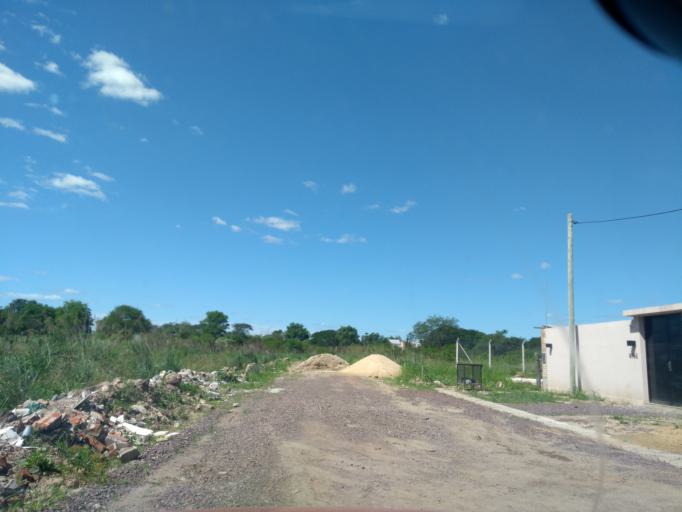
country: AR
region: Chaco
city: Resistencia
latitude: -27.4198
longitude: -58.9484
